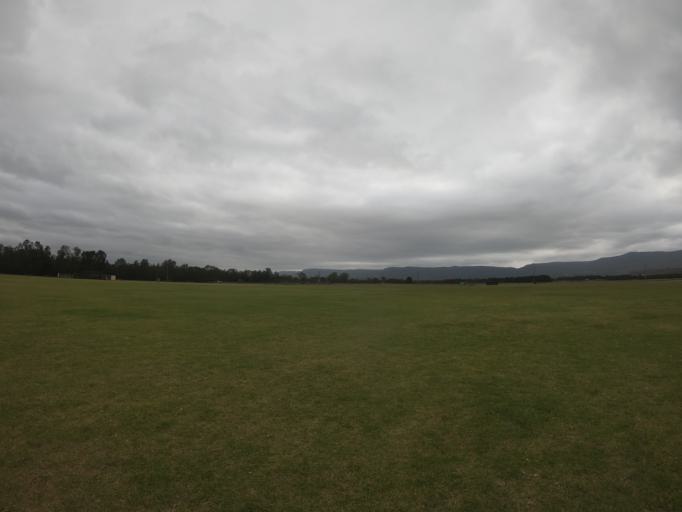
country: AU
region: New South Wales
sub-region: Wollongong
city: Berkeley
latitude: -34.4826
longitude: 150.8353
